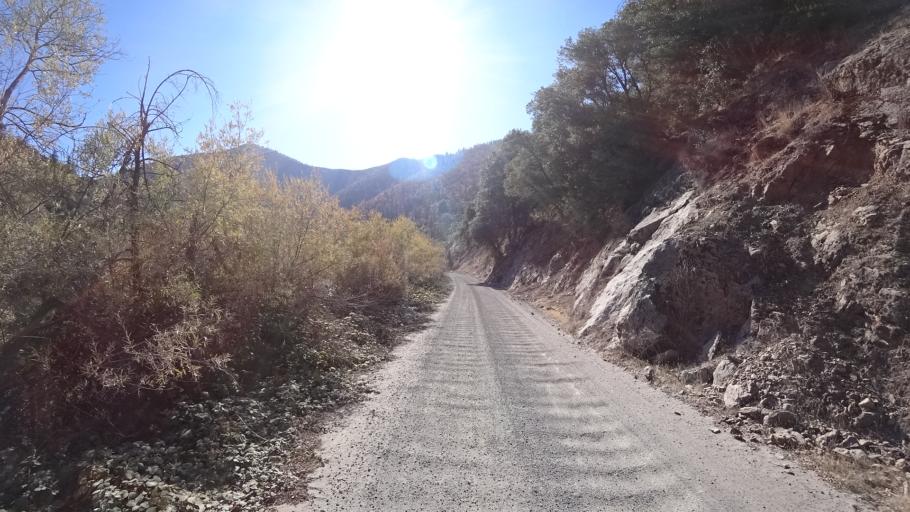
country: US
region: California
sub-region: Siskiyou County
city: Yreka
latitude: 41.8302
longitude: -122.6619
